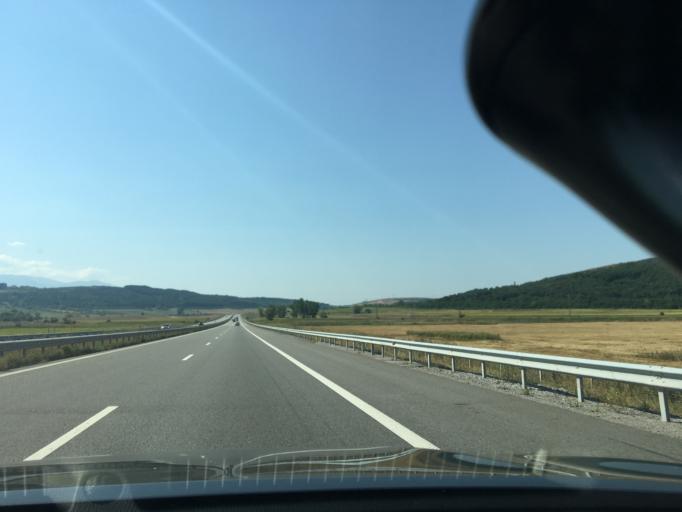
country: BG
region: Kyustendil
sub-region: Obshtina Bobovdol
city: Bobovdol
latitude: 42.4125
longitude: 23.1203
